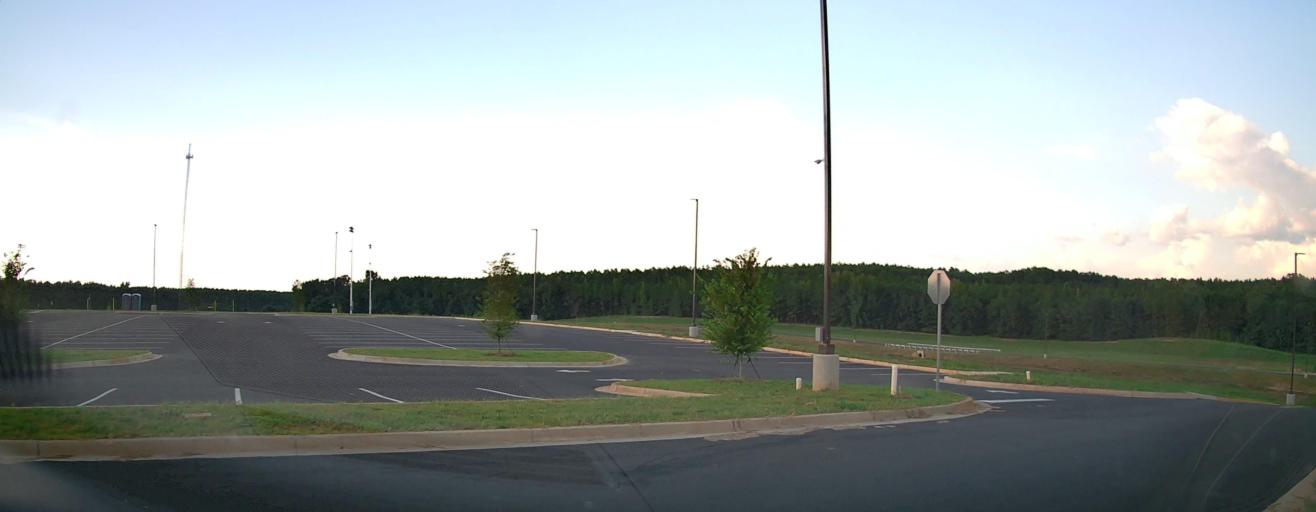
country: US
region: Georgia
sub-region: Peach County
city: Fort Valley
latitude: 32.5917
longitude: -83.8383
